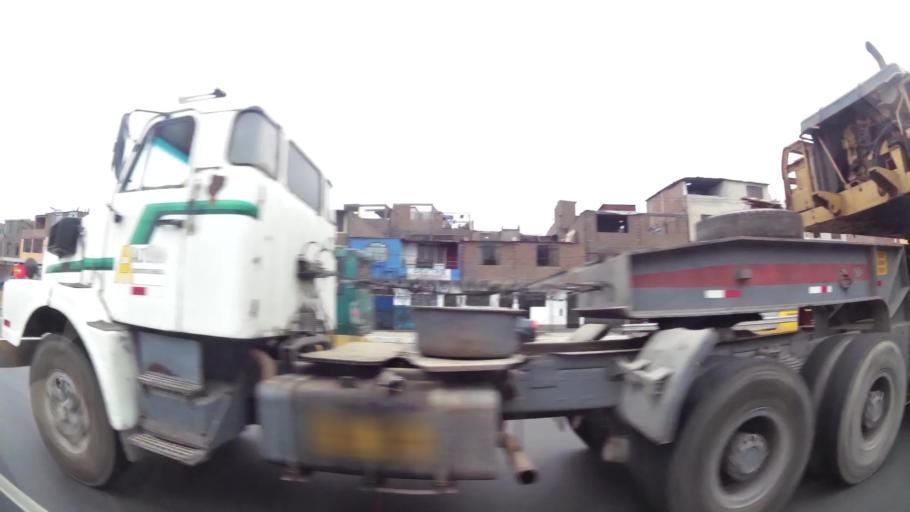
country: PE
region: Lima
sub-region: Lima
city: San Luis
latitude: -12.0819
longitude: -76.9791
